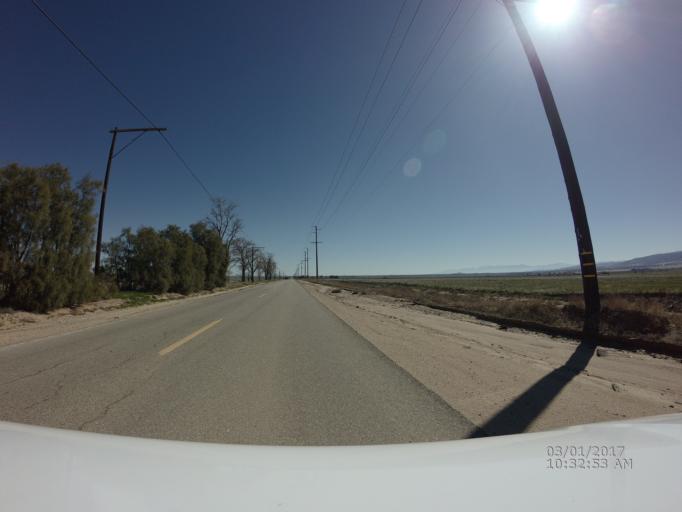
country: US
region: California
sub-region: Los Angeles County
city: Leona Valley
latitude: 34.6893
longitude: -118.2840
